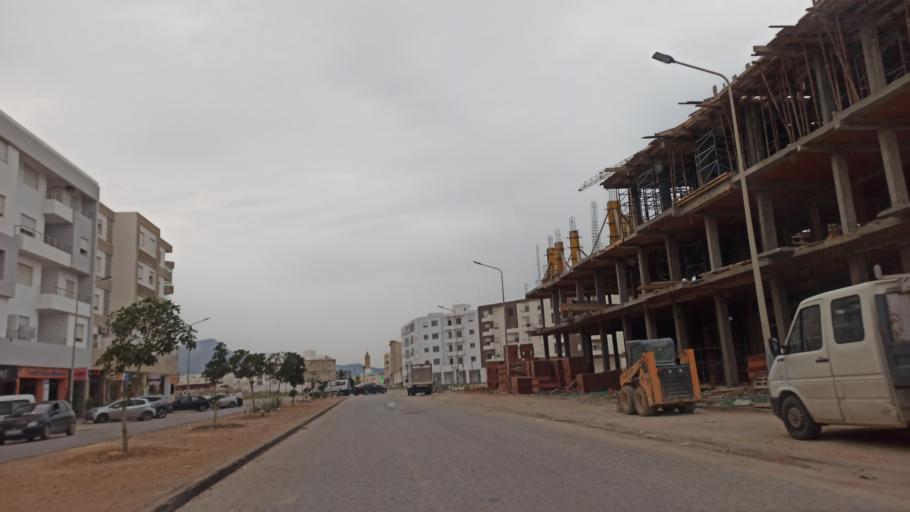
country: TN
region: Tunis
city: Hammam-Lif
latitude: 36.7050
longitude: 10.4152
